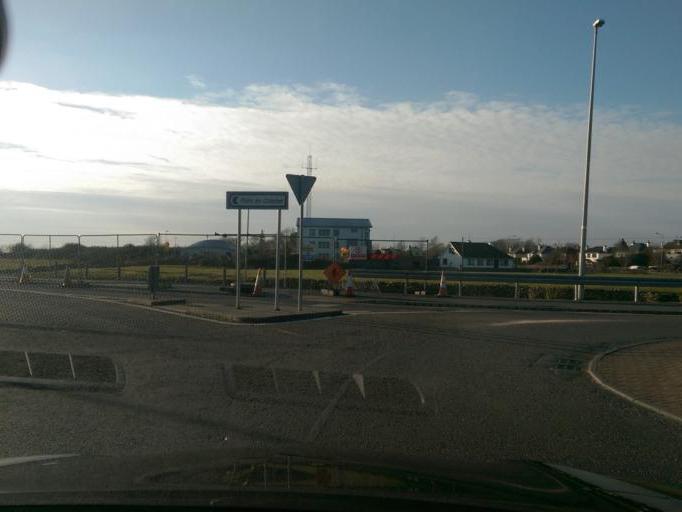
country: IE
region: Connaught
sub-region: County Galway
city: Oranmore
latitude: 53.2712
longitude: -8.9293
